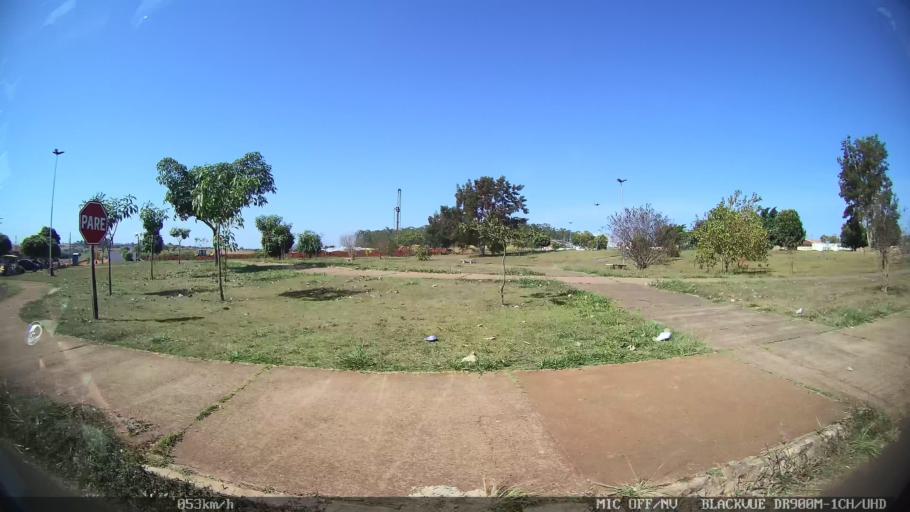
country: BR
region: Sao Paulo
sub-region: Batatais
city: Batatais
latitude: -20.8749
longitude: -47.5933
